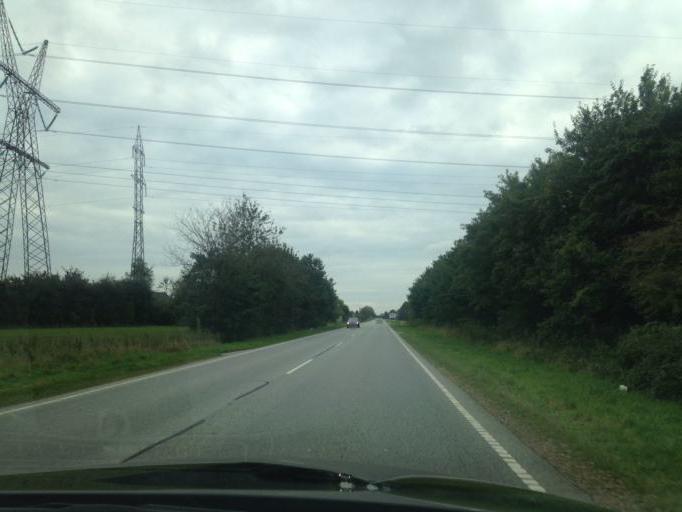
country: DK
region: South Denmark
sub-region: Haderslev Kommune
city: Vojens
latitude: 55.2540
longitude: 9.3480
